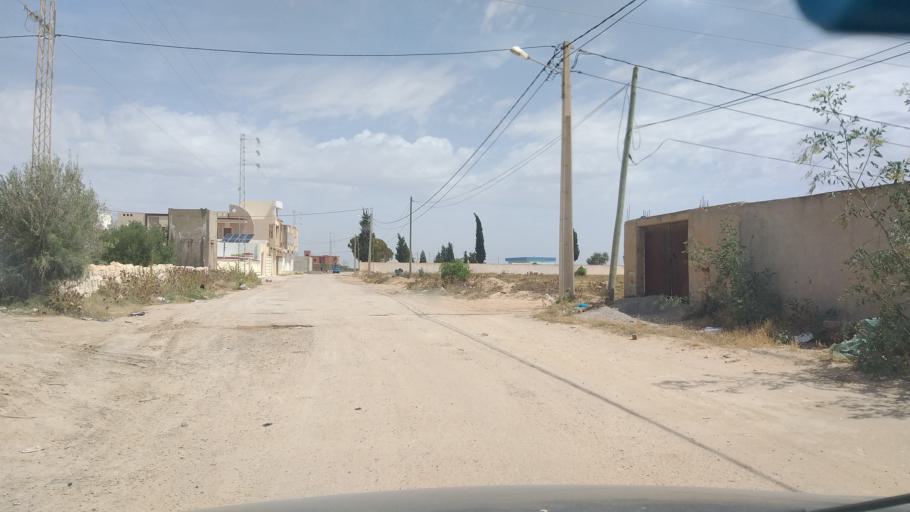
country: TN
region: Al Mahdiyah
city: El Jem
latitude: 35.3088
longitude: 10.7039
